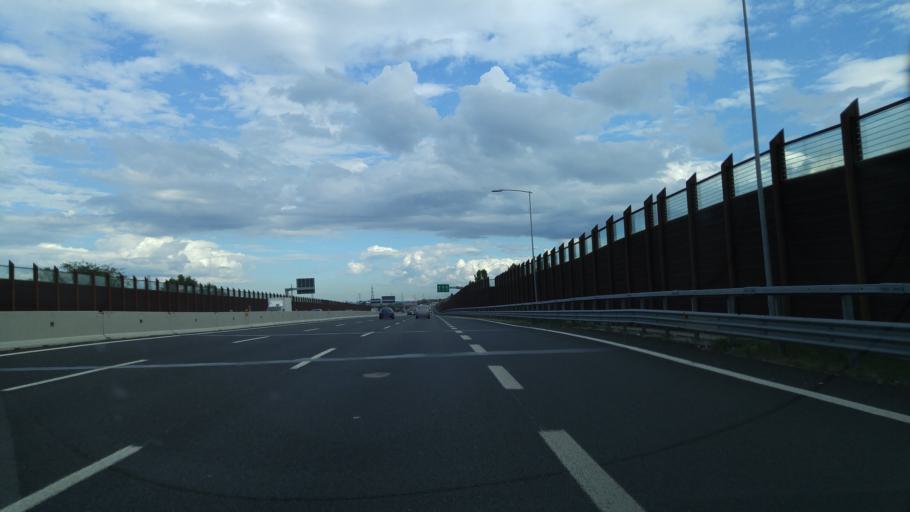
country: IT
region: Emilia-Romagna
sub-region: Provincia di Rimini
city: Rimini
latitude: 44.0337
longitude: 12.5715
